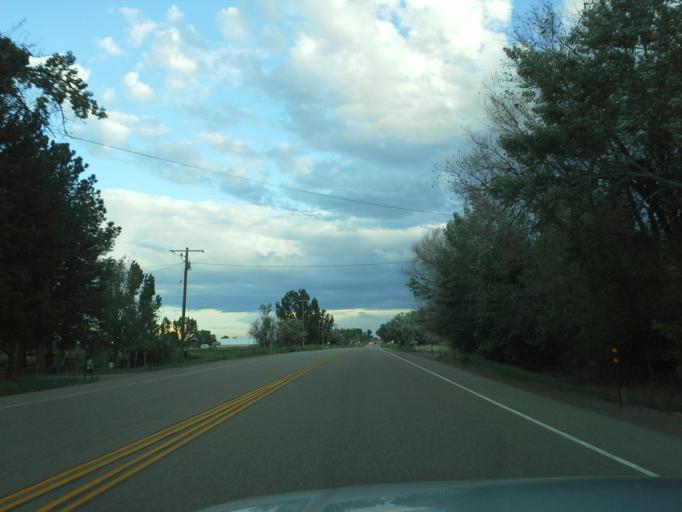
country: US
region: Wyoming
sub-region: Big Horn County
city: Basin
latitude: 44.3704
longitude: -108.0390
